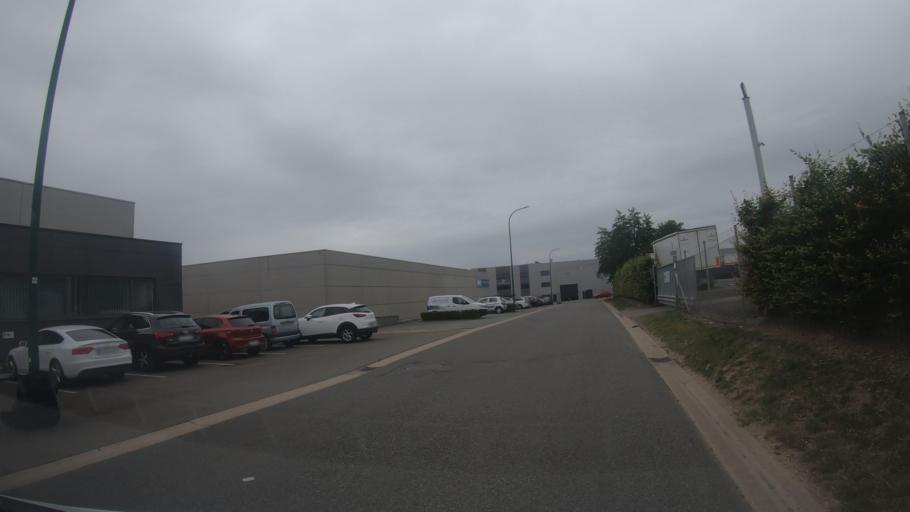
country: BE
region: Wallonia
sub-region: Province de Liege
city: Dison
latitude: 50.6295
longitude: 5.8838
